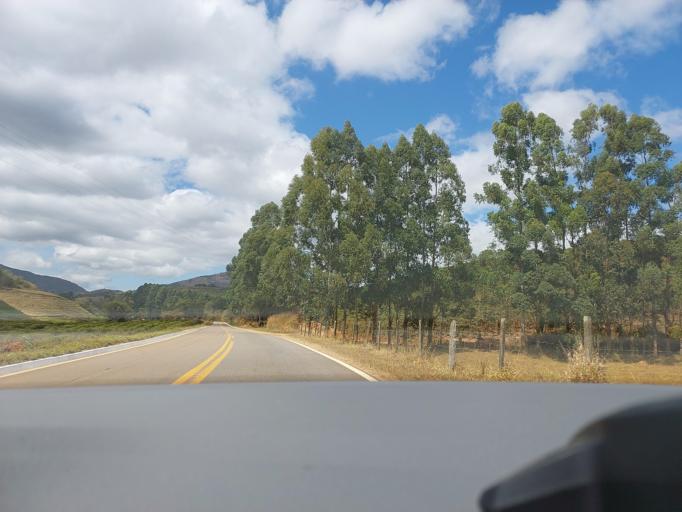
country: BR
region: Minas Gerais
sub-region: Visconde Do Rio Branco
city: Visconde do Rio Branco
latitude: -20.9427
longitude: -42.6273
